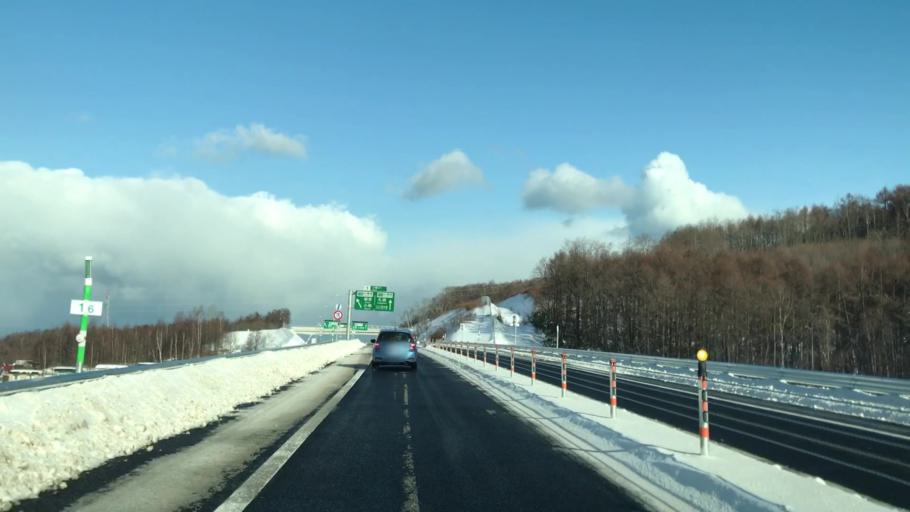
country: JP
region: Hokkaido
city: Otaru
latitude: 43.1610
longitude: 141.0552
